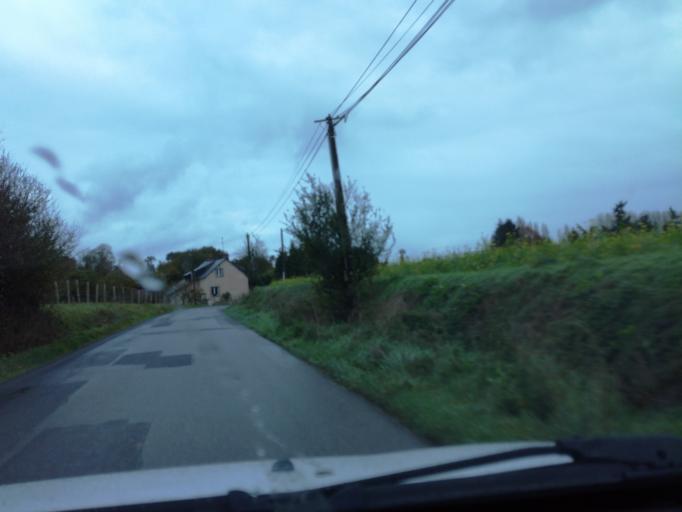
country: FR
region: Brittany
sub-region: Departement d'Ille-et-Vilaine
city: Montgermont
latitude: 48.1749
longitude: -1.7041
